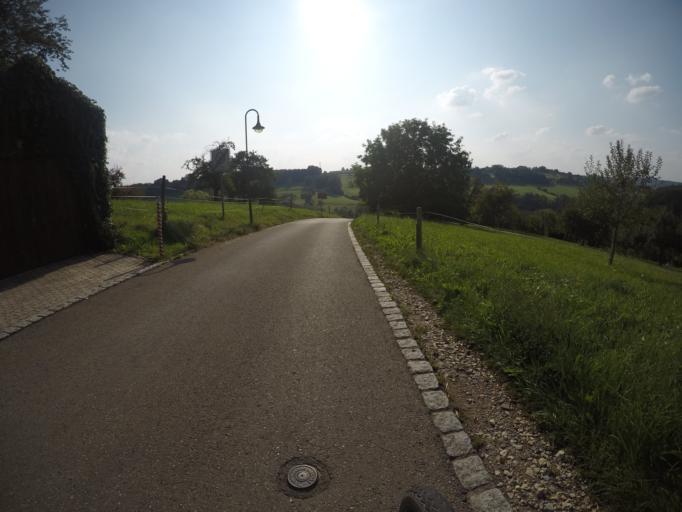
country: DE
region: Baden-Wuerttemberg
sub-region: Tuebingen Region
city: Pliezhausen
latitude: 48.5408
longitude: 9.2251
